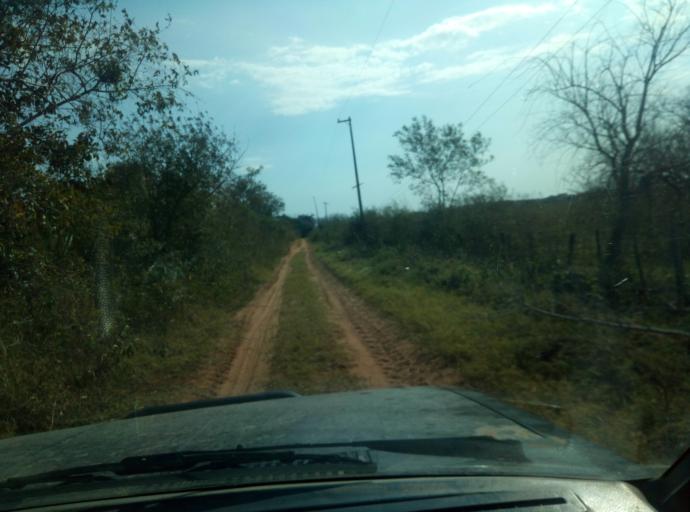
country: PY
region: Caaguazu
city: Doctor Cecilio Baez
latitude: -25.1428
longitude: -56.2513
